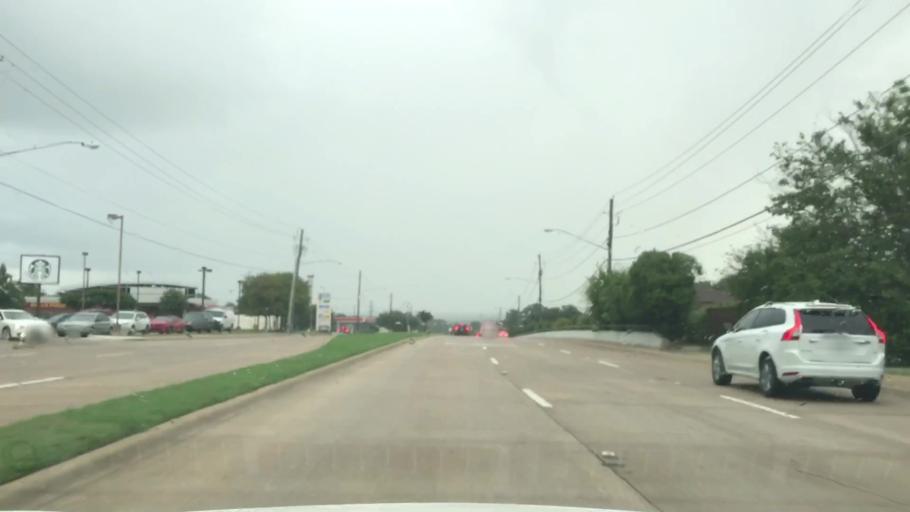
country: US
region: Texas
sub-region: Dallas County
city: Richardson
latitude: 32.8957
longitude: -96.7395
